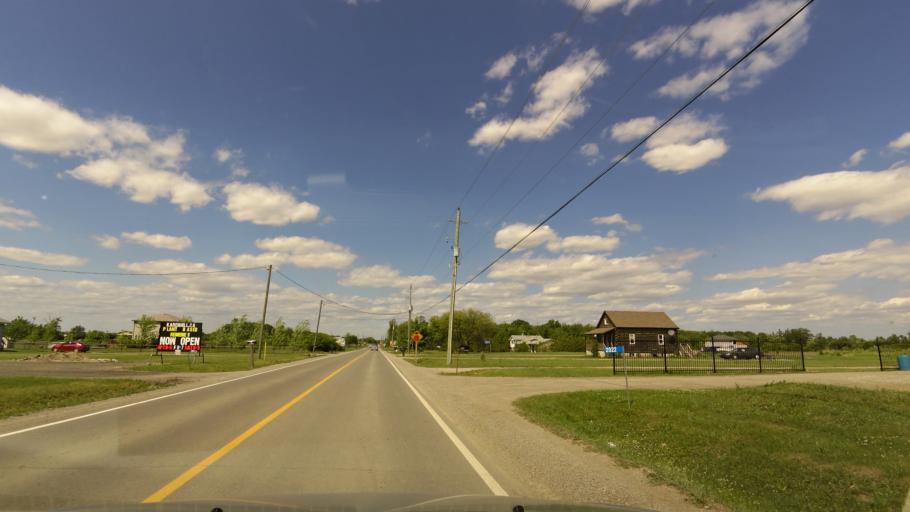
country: CA
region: Ontario
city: Brantford
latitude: 43.0831
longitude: -80.1086
